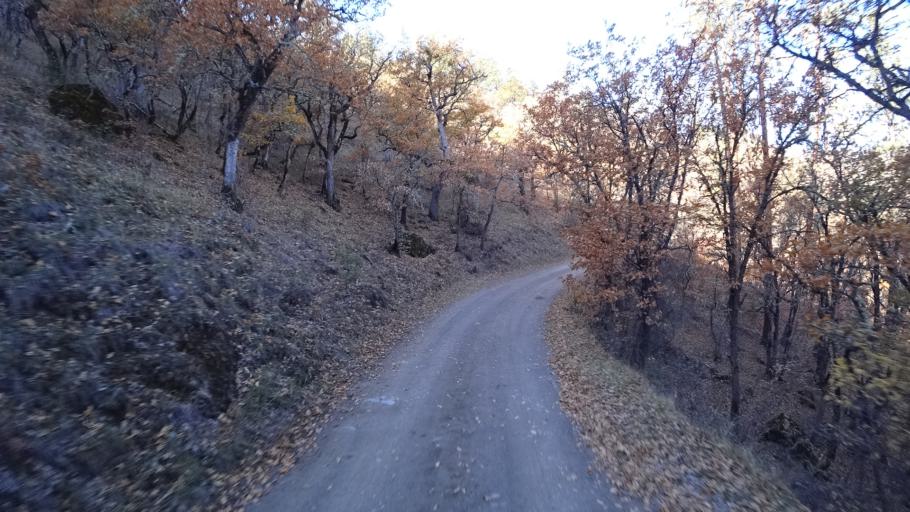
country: US
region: California
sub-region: Siskiyou County
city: Yreka
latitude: 41.8671
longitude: -122.8135
